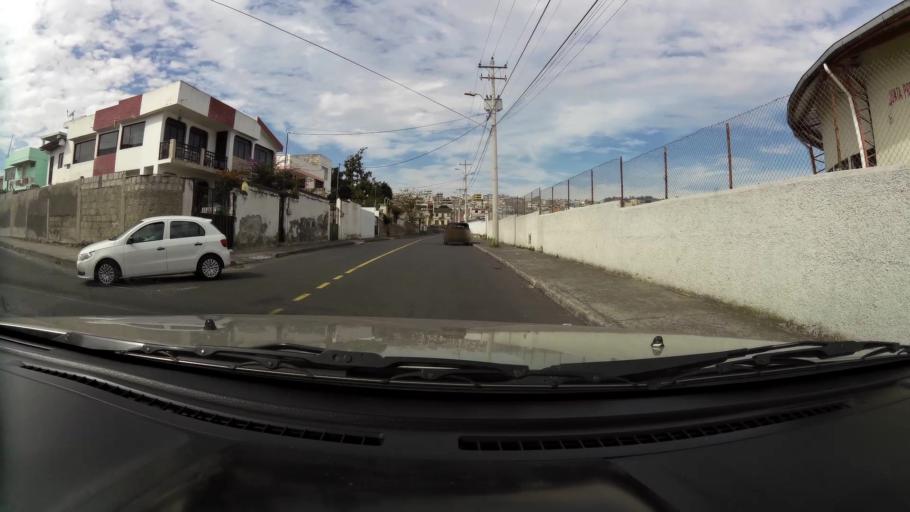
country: EC
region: Tungurahua
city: Ambato
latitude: -1.2442
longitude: -78.6241
